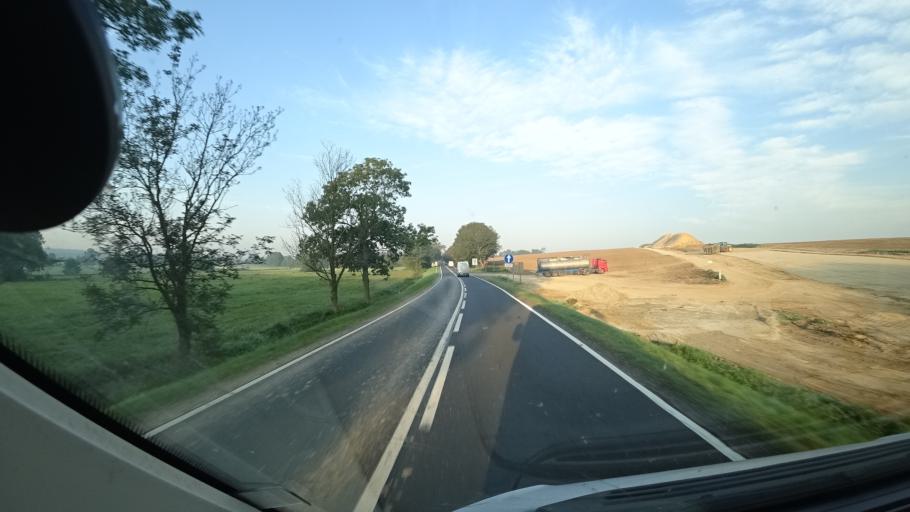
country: PL
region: Silesian Voivodeship
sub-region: Powiat gliwicki
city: Rudziniec
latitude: 50.3888
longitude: 18.3929
